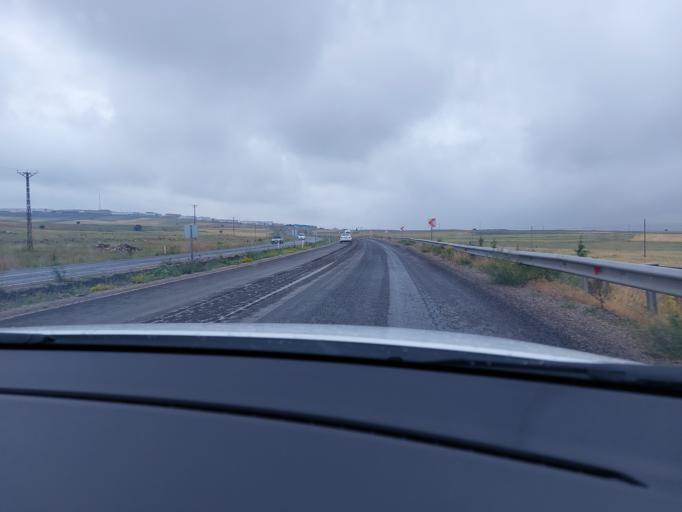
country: TR
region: Nevsehir
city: Dobada
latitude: 38.5397
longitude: 34.4538
